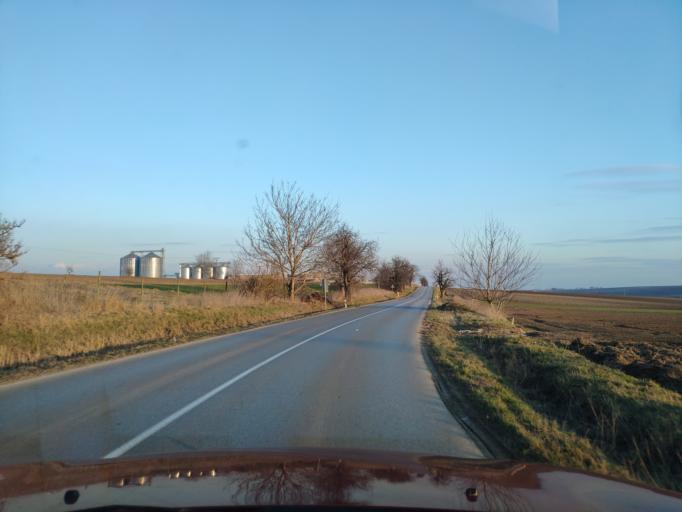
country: SK
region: Nitriansky
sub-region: Okres Nitra
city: Nitra
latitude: 48.2448
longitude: 18.0337
